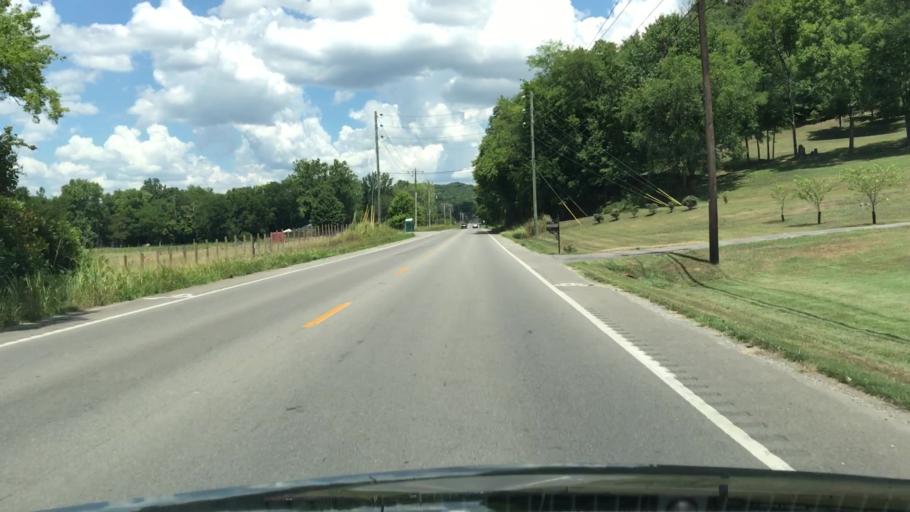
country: US
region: Tennessee
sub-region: Williamson County
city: Nolensville
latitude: 35.8862
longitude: -86.6634
